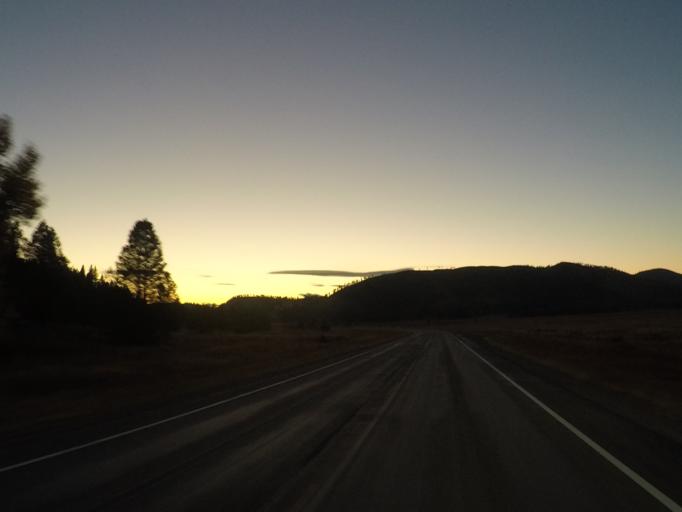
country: US
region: Montana
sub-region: Missoula County
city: Seeley Lake
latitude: 47.0301
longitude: -113.2490
